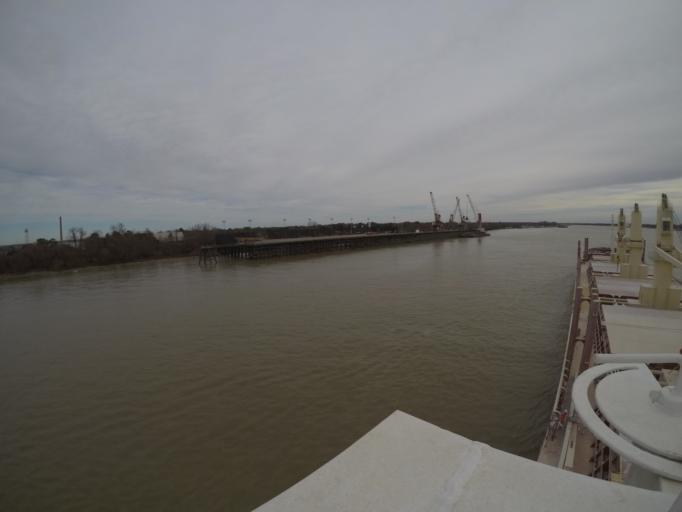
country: US
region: Louisiana
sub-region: Saint John the Baptist Parish
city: Edgard
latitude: 30.0524
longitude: -90.5672
